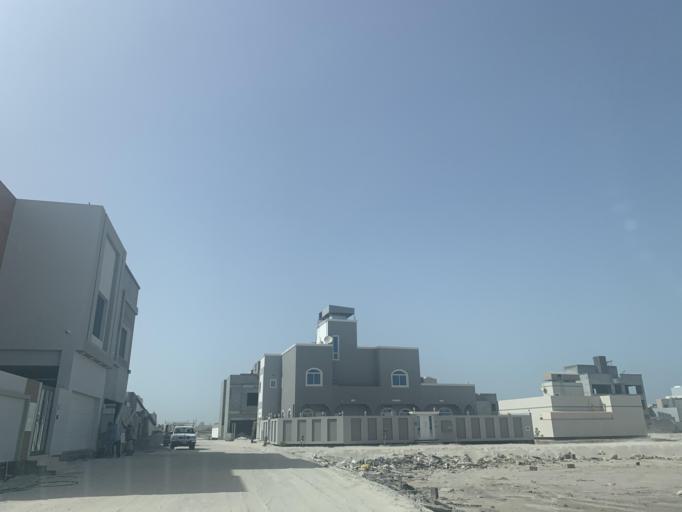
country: BH
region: Northern
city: Sitrah
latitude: 26.1677
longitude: 50.6192
